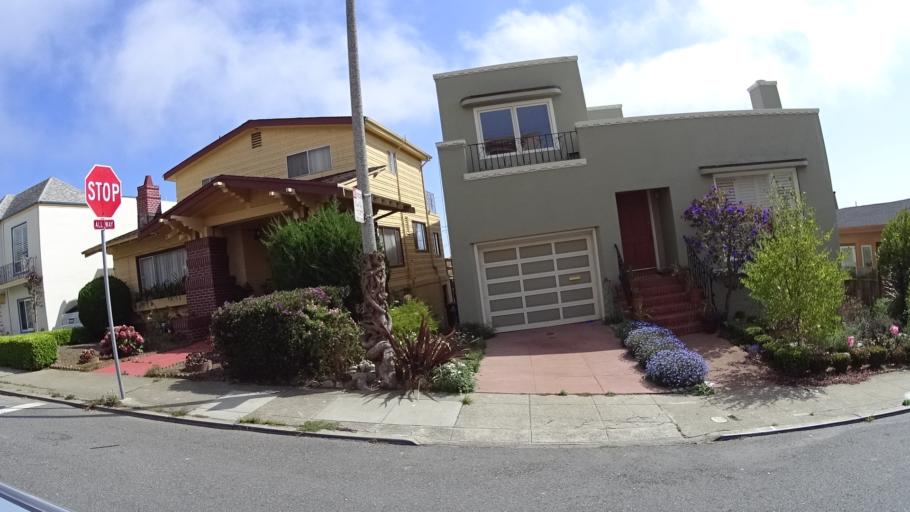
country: US
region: California
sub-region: San Mateo County
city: Daly City
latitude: 37.7287
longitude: -122.4600
